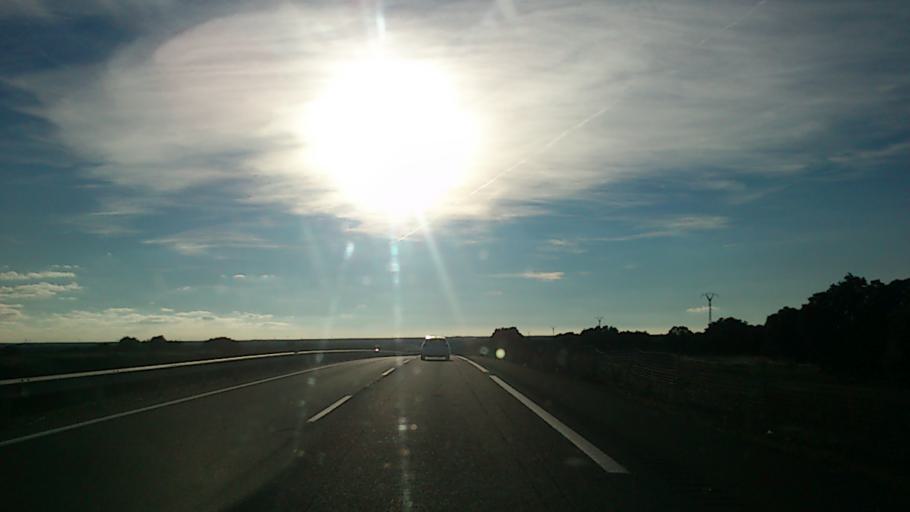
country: ES
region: Castille-La Mancha
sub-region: Provincia de Guadalajara
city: Mirabueno
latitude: 40.9412
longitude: -2.6989
